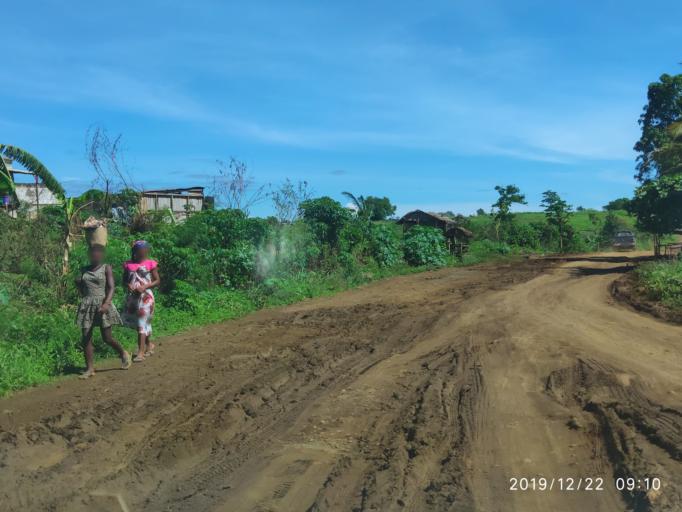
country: MG
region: Diana
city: Sadjoavato
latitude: -12.7629
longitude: 49.2353
